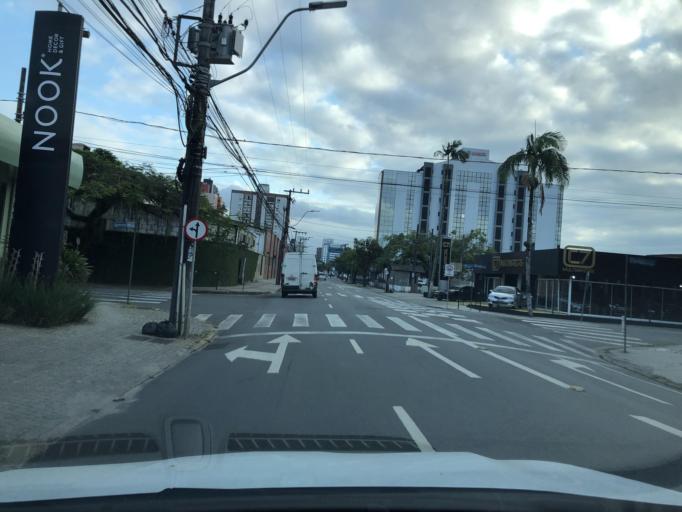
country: BR
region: Santa Catarina
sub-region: Joinville
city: Joinville
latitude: -26.2905
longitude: -48.8499
